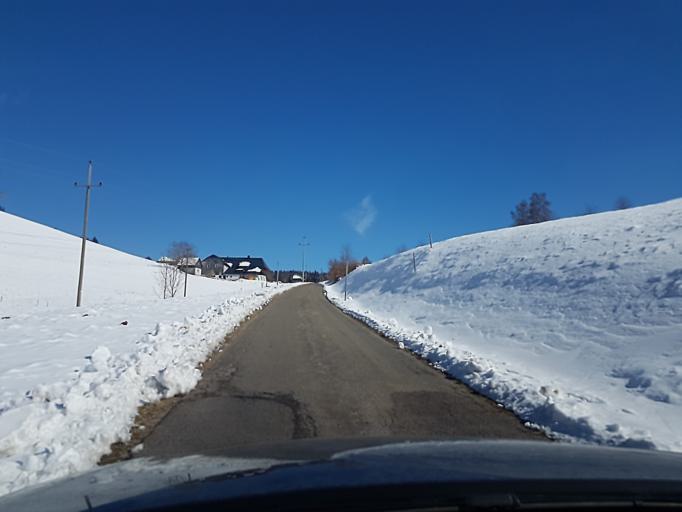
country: DE
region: Baden-Wuerttemberg
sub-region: Freiburg Region
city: Triberg im Schwarzwald
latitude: 48.1411
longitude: 8.2522
